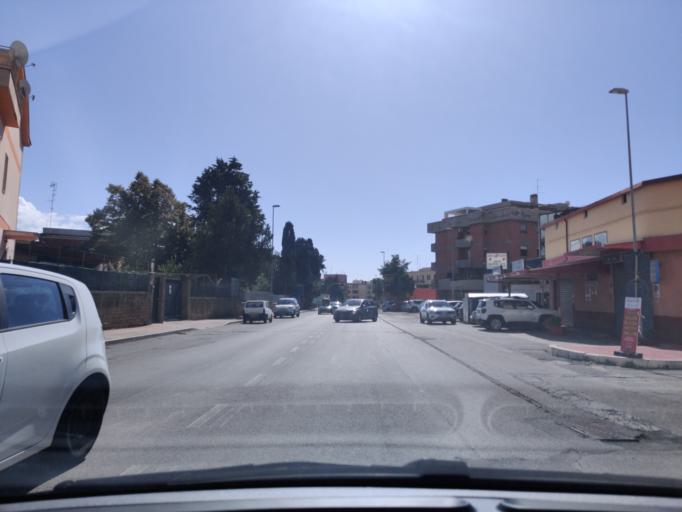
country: IT
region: Latium
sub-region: Citta metropolitana di Roma Capitale
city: Civitavecchia
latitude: 42.0914
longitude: 11.8070
